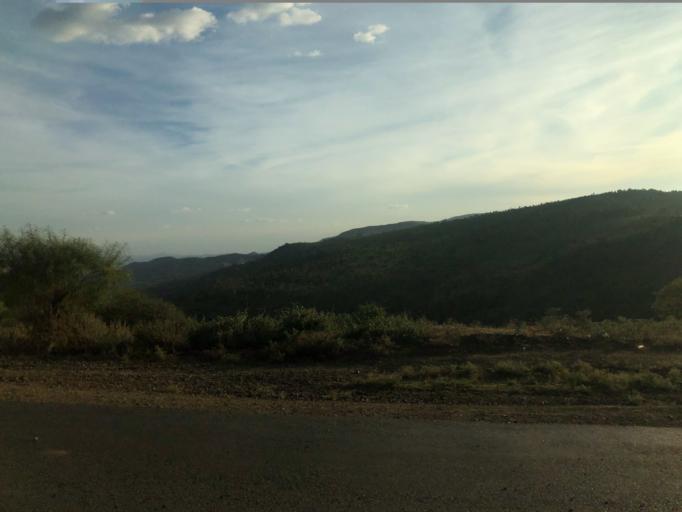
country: ET
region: Southern Nations, Nationalities, and People's Region
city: Konso
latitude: 5.3328
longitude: 37.4146
